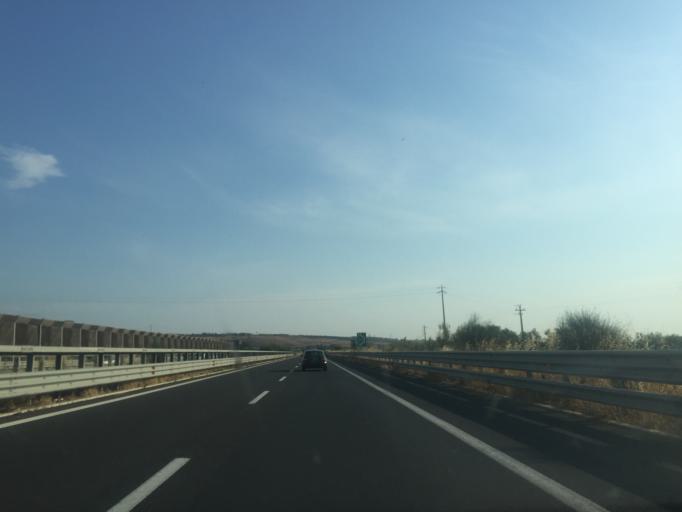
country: IT
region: Sicily
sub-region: Provincia di Siracusa
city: Carlentini
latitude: 37.3479
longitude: 15.0444
